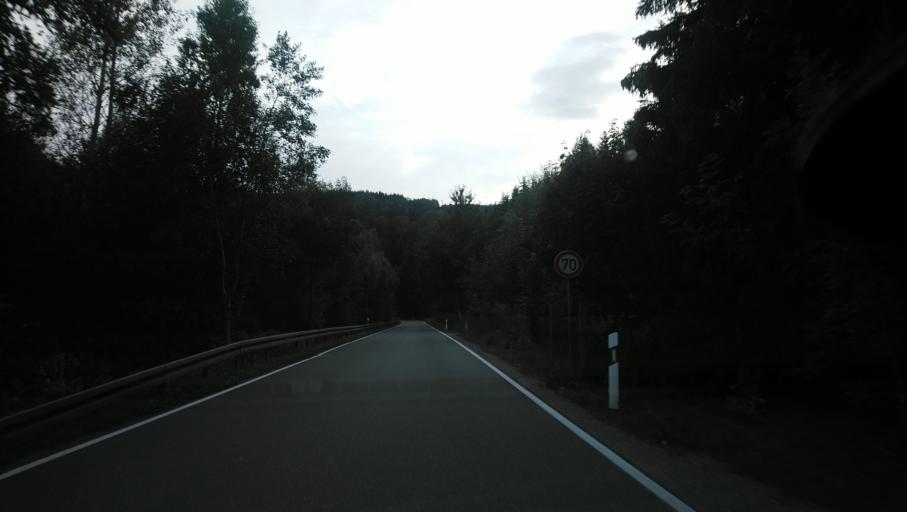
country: DE
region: Saxony
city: Annaberg-Buchholz
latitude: 50.5900
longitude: 13.0020
